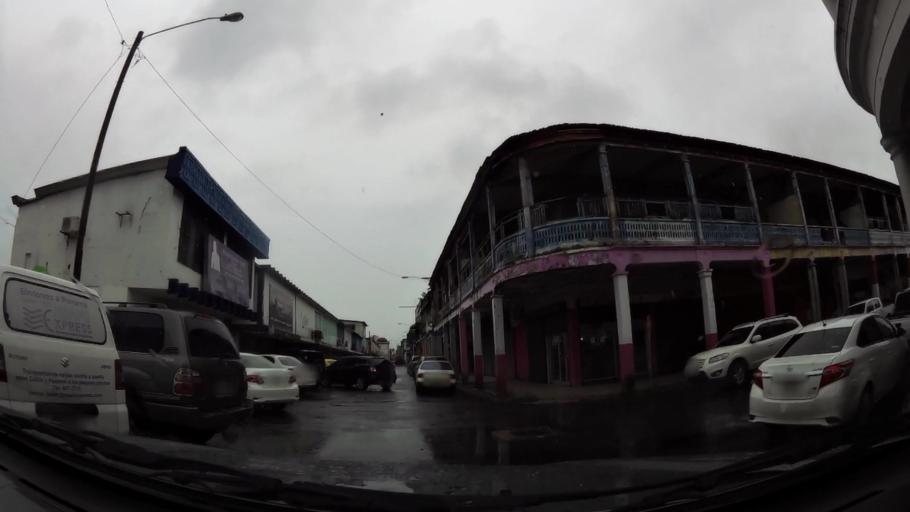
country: PA
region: Colon
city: Colon
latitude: 9.3559
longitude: -79.9044
